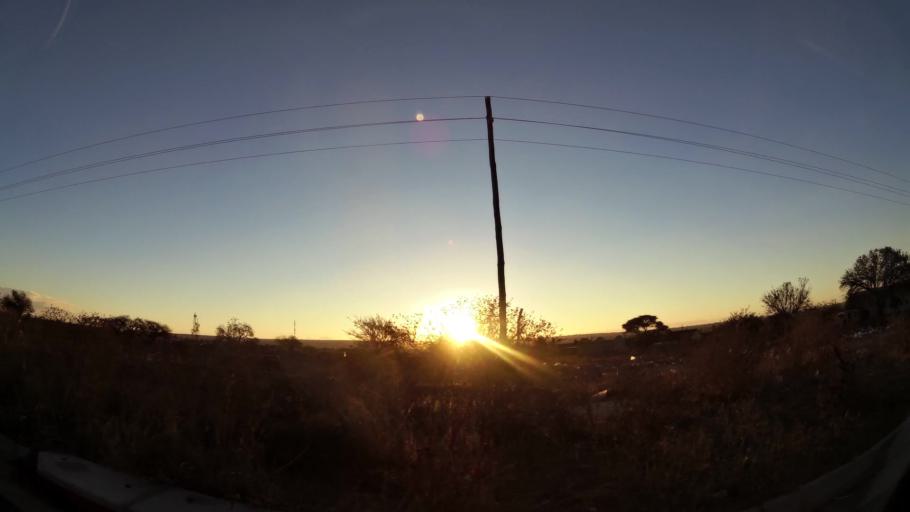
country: ZA
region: Limpopo
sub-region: Capricorn District Municipality
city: Polokwane
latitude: -23.8583
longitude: 29.3753
